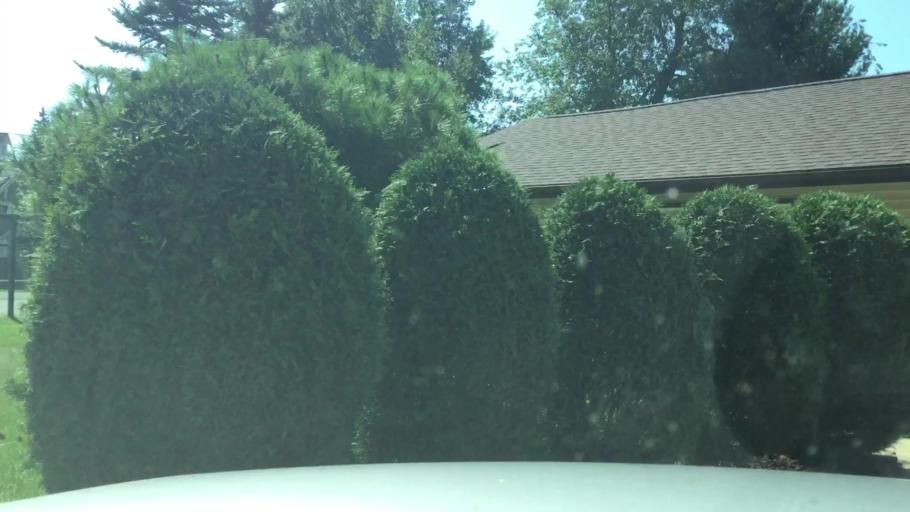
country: US
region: Michigan
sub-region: Lenawee County
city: Manitou Beach-Devils Lake
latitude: 41.9851
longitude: -84.2816
